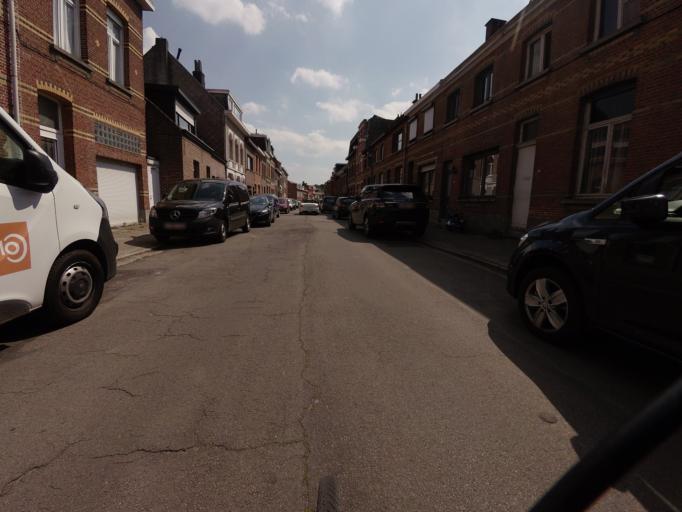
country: BE
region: Flanders
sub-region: Provincie Antwerpen
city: Hove
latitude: 51.1642
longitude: 4.4684
